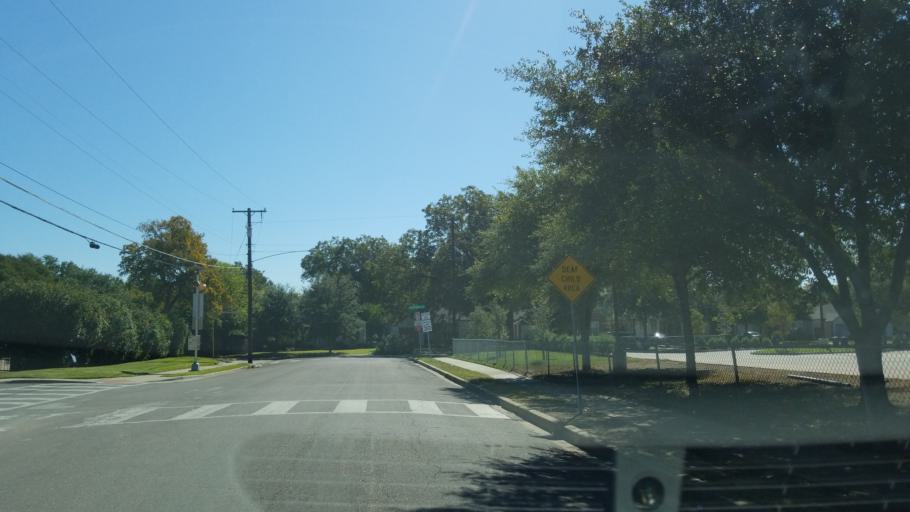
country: US
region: Texas
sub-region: Dallas County
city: Highland Park
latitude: 32.8069
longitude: -96.7484
